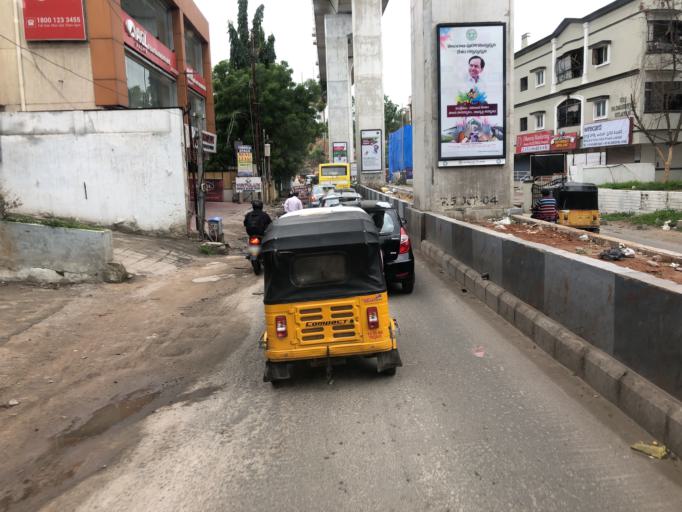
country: IN
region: Telangana
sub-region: Rangareddi
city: Kukatpalli
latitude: 17.4304
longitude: 78.4219
